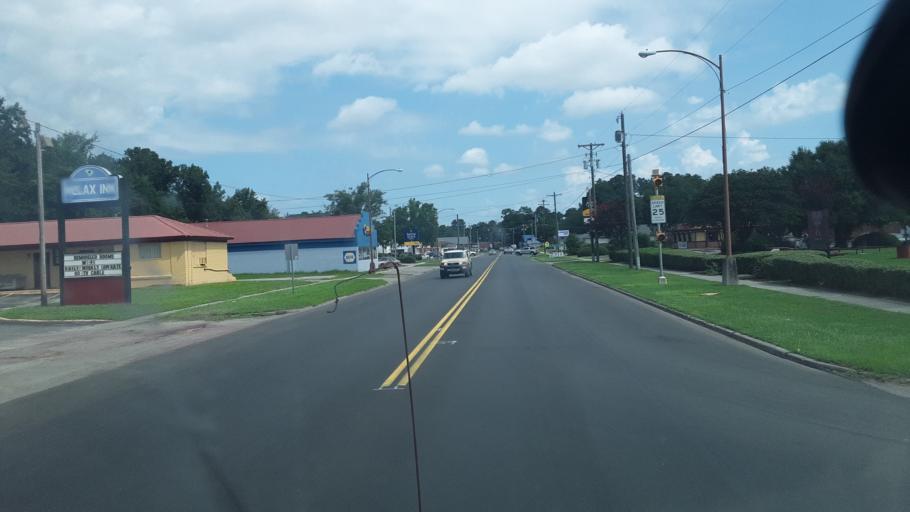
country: US
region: South Carolina
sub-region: Bamberg County
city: Bamberg
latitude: 33.2997
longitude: -81.0342
